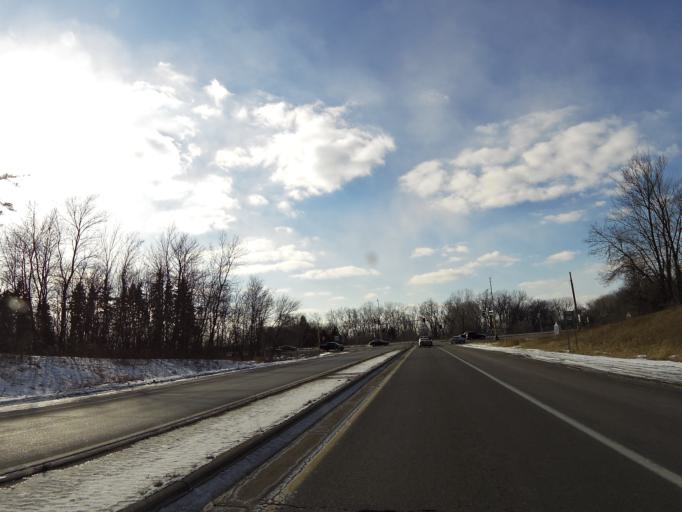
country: US
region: Minnesota
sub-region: Dakota County
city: Mendota Heights
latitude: 44.8646
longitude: -93.1282
